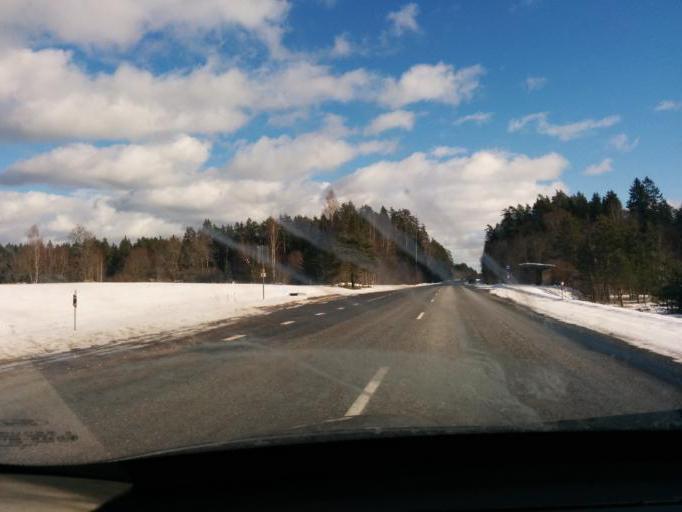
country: LV
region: Jaunpiebalga
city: Jaunpiebalga
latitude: 57.2388
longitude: 26.2729
